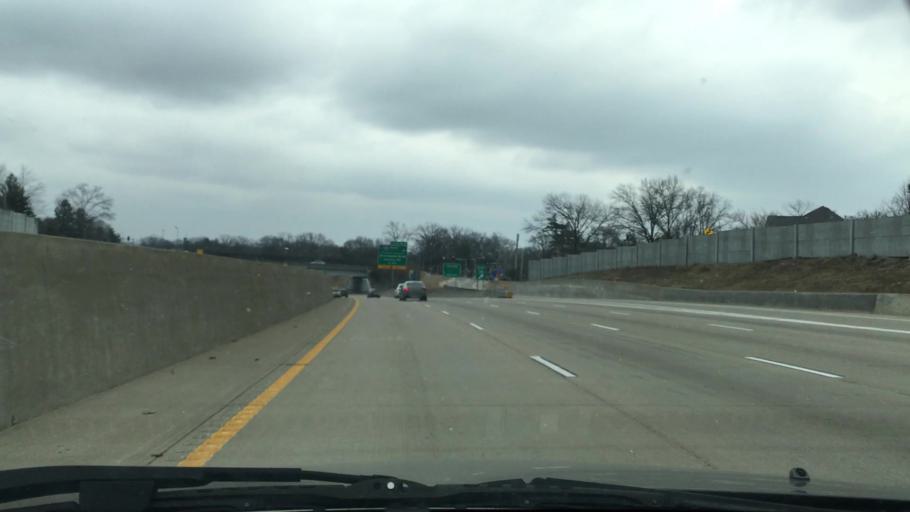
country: US
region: Missouri
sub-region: Saint Louis County
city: Brentwood
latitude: 38.6301
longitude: -90.3654
